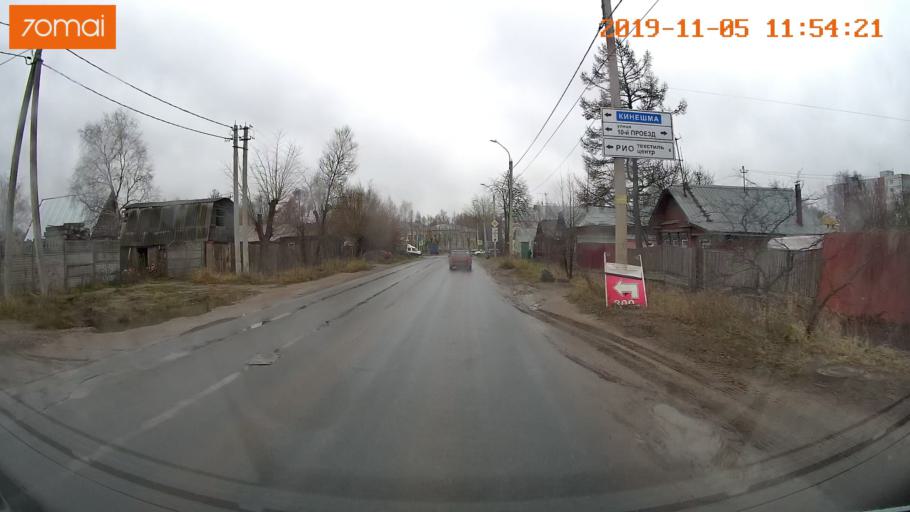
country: RU
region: Ivanovo
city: Bogorodskoye
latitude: 56.9910
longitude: 41.0313
